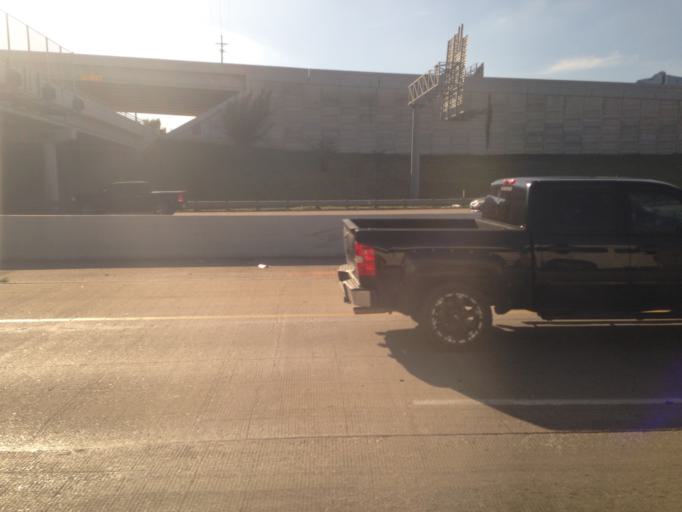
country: US
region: Texas
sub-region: Tarrant County
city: Fort Worth
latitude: 32.7512
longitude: -97.3196
